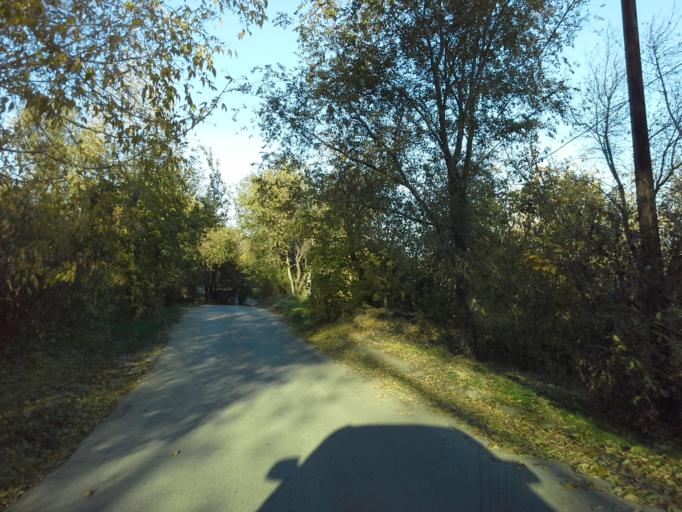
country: RU
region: Volgograd
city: Vodstroy
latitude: 48.8172
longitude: 44.6399
